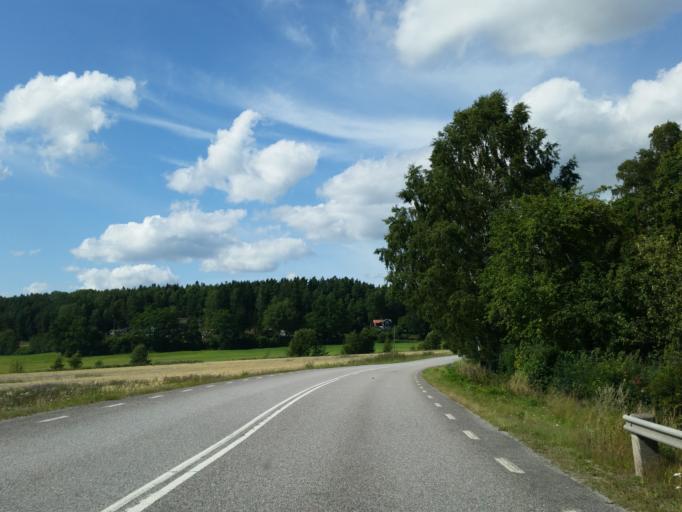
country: SE
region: Soedermanland
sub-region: Trosa Kommun
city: Vagnharad
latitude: 58.9905
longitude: 17.6196
